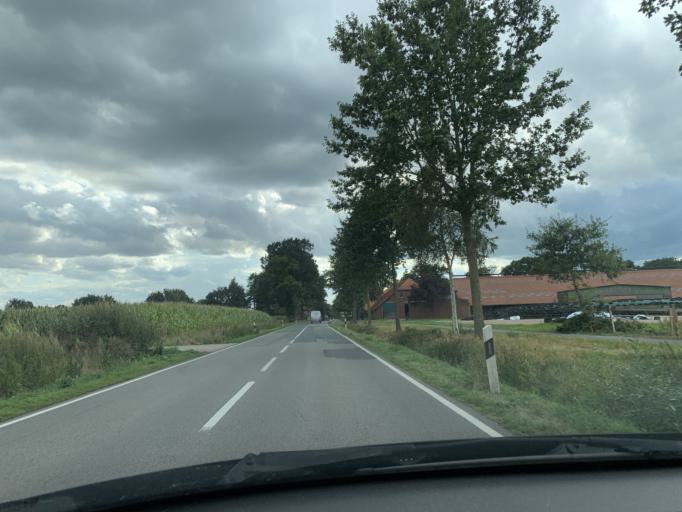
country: DE
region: Lower Saxony
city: Wiefelstede
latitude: 53.2875
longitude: 8.0300
